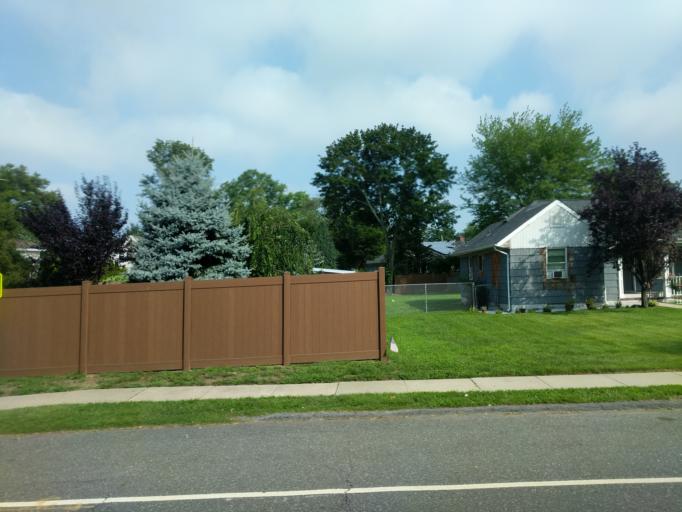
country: US
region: New York
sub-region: Nassau County
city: Malverne
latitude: 40.6790
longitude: -73.6662
